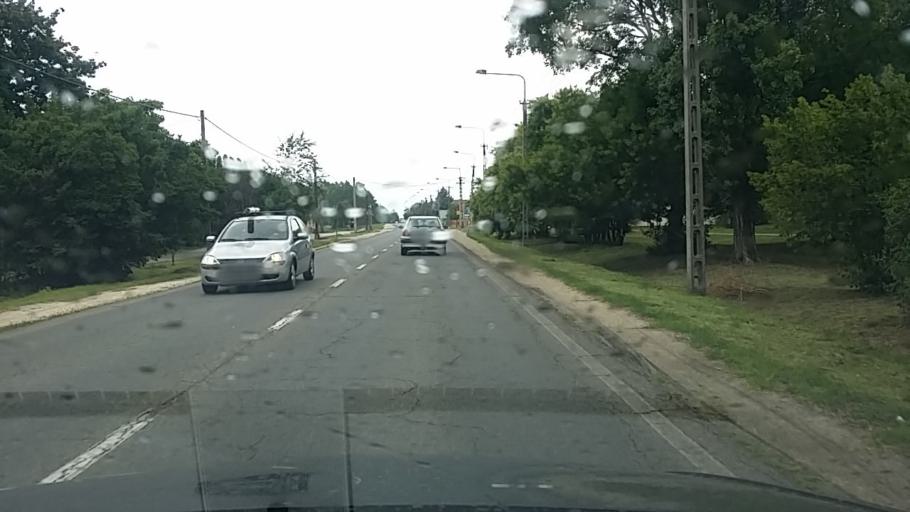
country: HU
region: Pest
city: Orkeny
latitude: 47.1298
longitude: 19.4232
